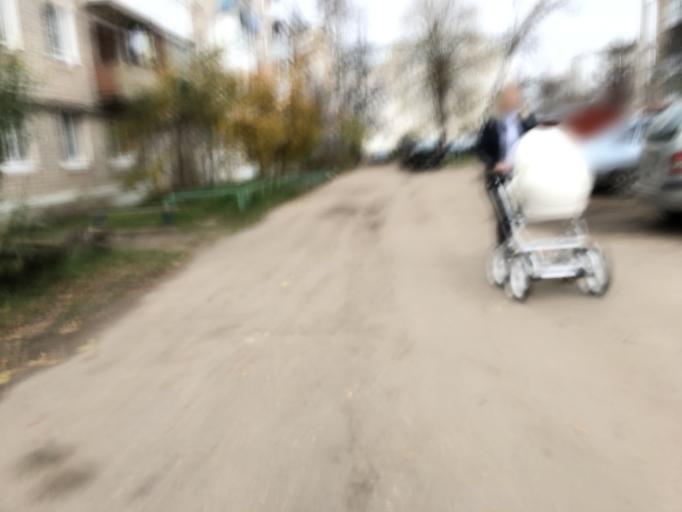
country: RU
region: Tverskaya
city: Rzhev
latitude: 56.2499
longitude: 34.3245
